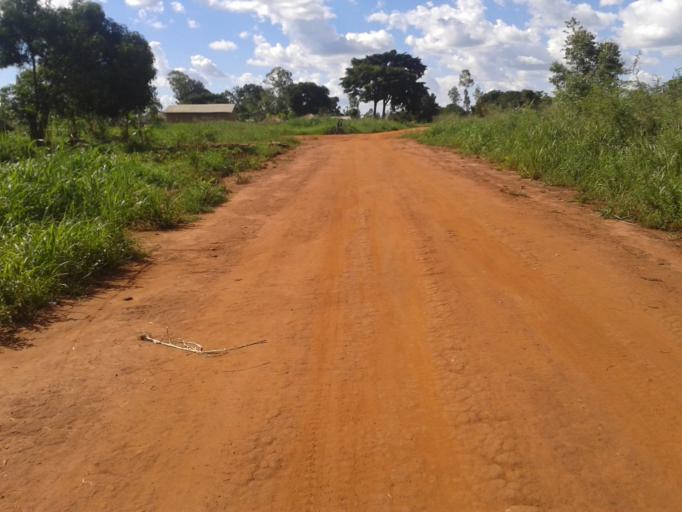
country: UG
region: Northern Region
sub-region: Gulu District
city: Gulu
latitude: 2.7698
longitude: 32.3210
